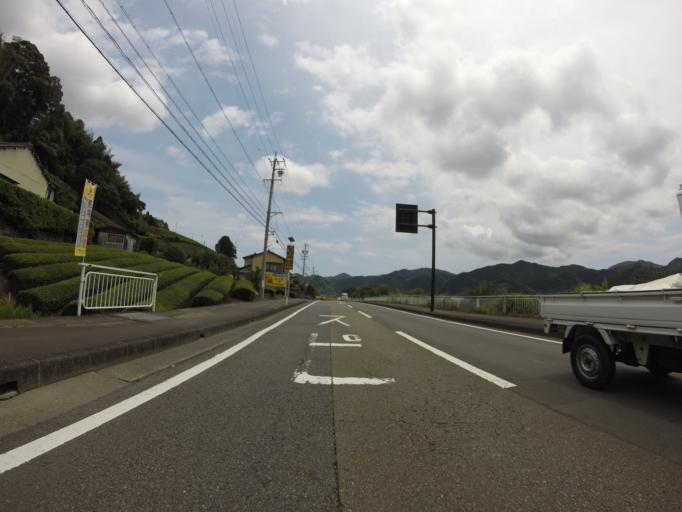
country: JP
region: Shizuoka
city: Shizuoka-shi
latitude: 34.9890
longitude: 138.3021
